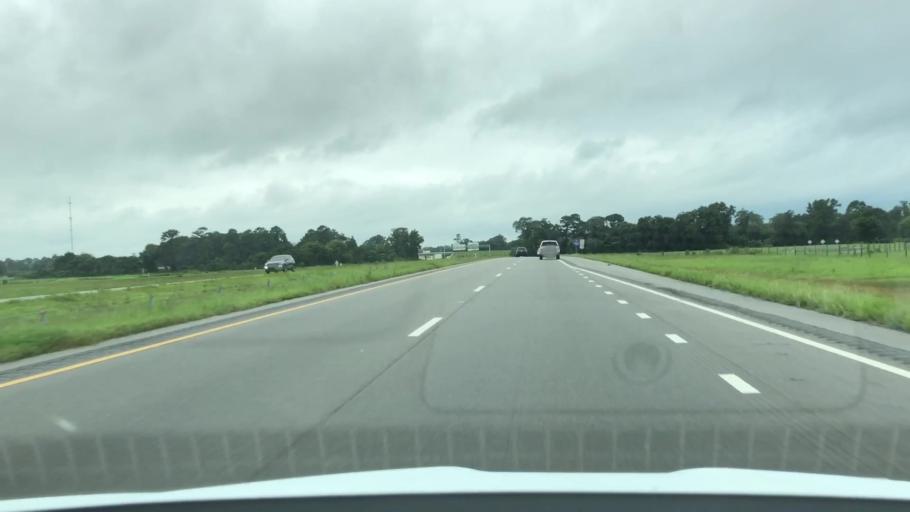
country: US
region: North Carolina
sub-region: Lenoir County
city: La Grange
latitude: 35.3053
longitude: -77.8197
